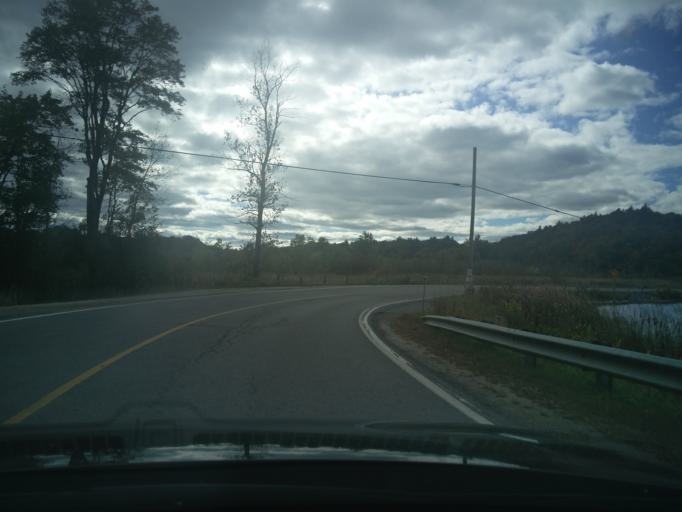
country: CA
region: Ontario
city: Perth
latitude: 44.6432
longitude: -76.5097
